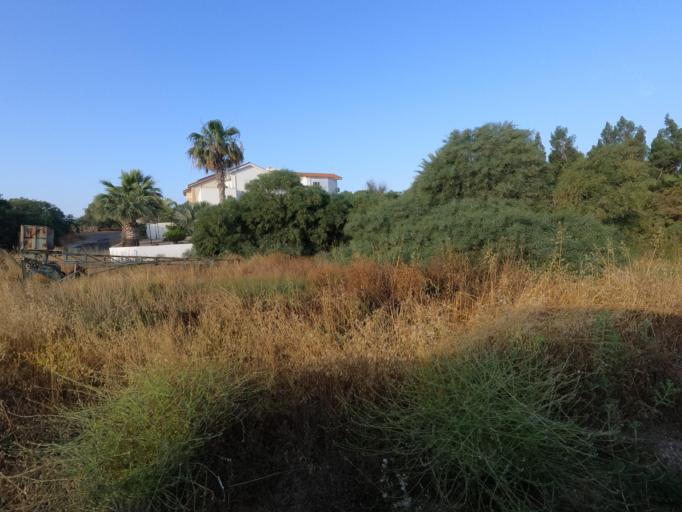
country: CY
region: Ammochostos
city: Paralimni
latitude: 35.0268
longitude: 33.9642
